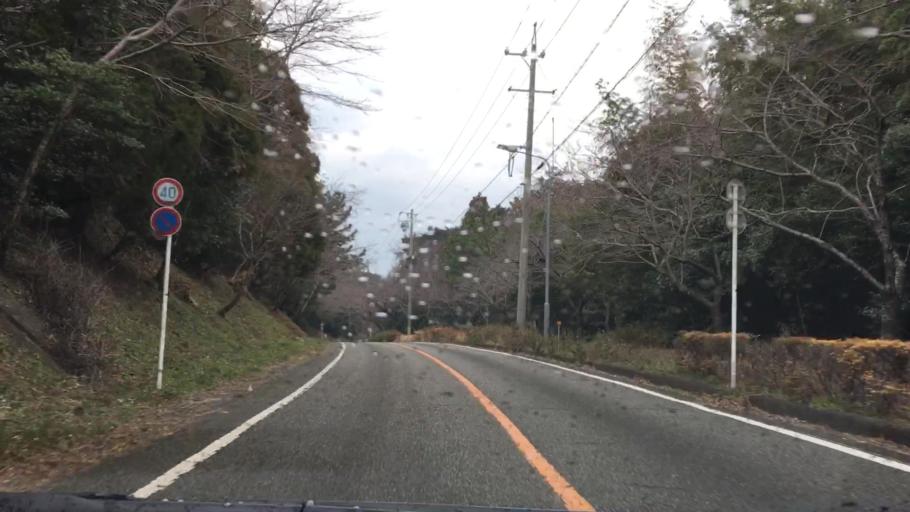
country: JP
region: Aichi
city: Tahara
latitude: 34.6751
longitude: 137.2491
